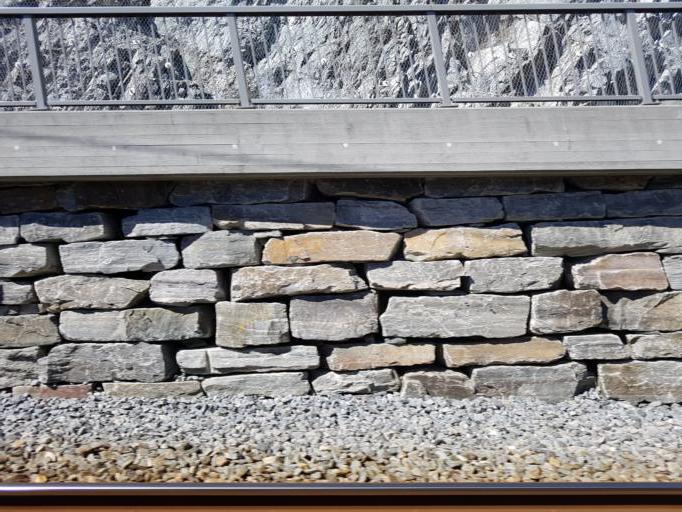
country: NO
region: Hordaland
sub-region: Bergen
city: Ytrebygda
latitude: 60.2953
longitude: 5.2689
